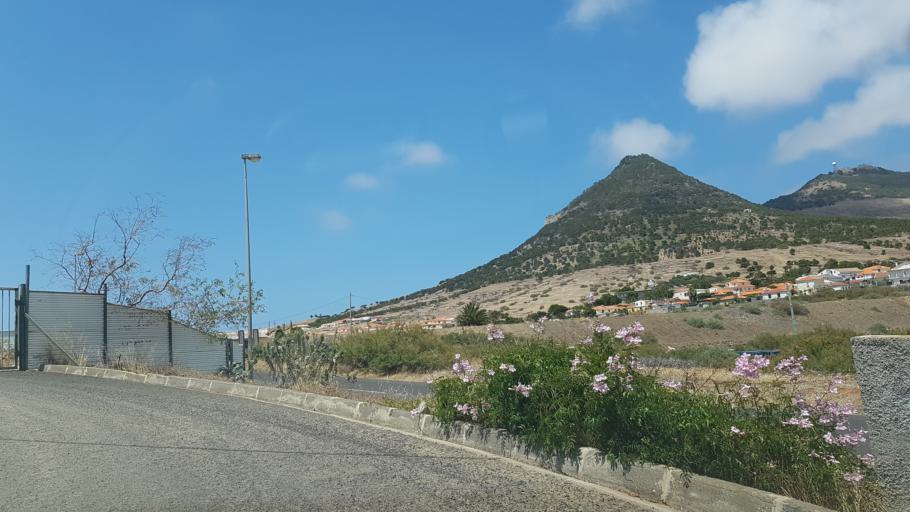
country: PT
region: Madeira
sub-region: Porto Santo
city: Vila de Porto Santo
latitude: 33.0680
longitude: -16.3420
